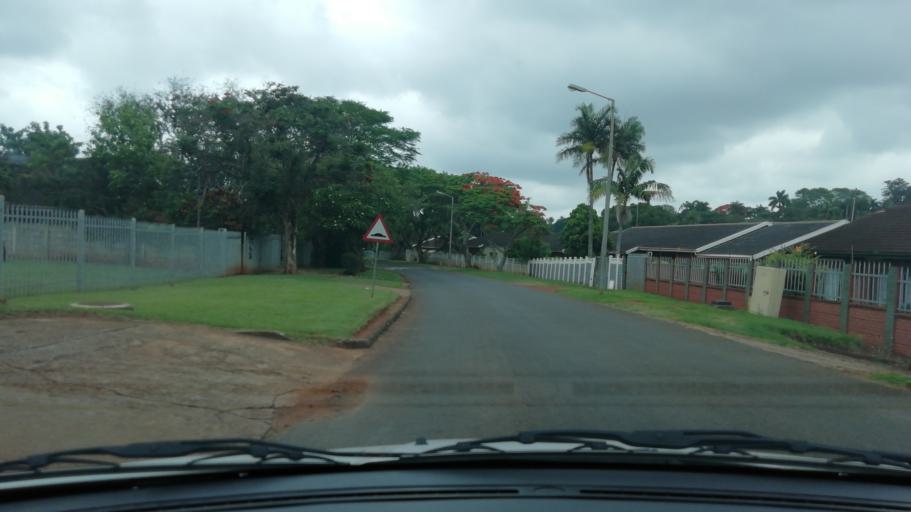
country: ZA
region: KwaZulu-Natal
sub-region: uThungulu District Municipality
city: Empangeni
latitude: -28.7598
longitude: 31.8995
